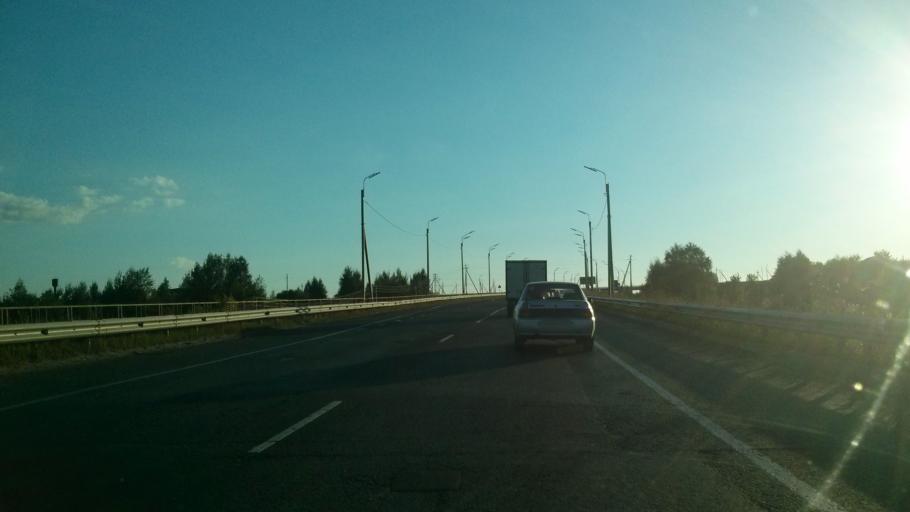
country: RU
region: Vladimir
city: Murom
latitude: 55.6193
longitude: 42.0333
